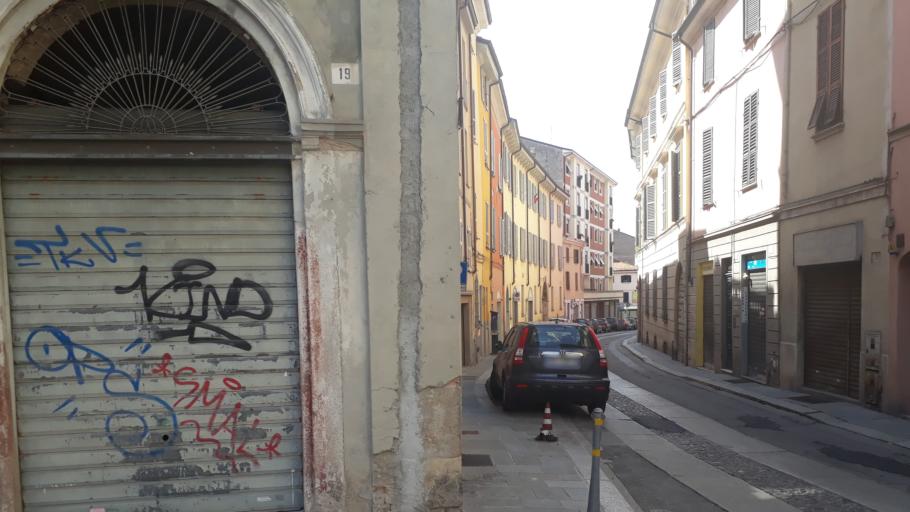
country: IT
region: Emilia-Romagna
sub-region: Provincia di Piacenza
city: Piacenza
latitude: 45.0540
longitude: 9.6884
